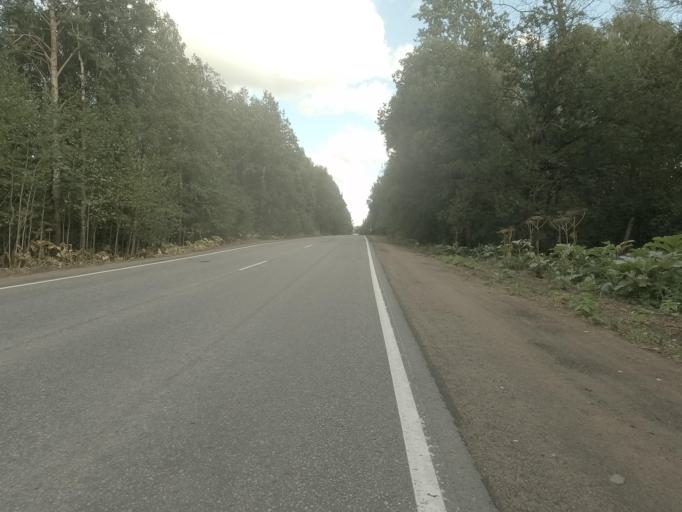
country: RU
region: Leningrad
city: Shcheglovo
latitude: 60.0199
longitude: 30.7360
